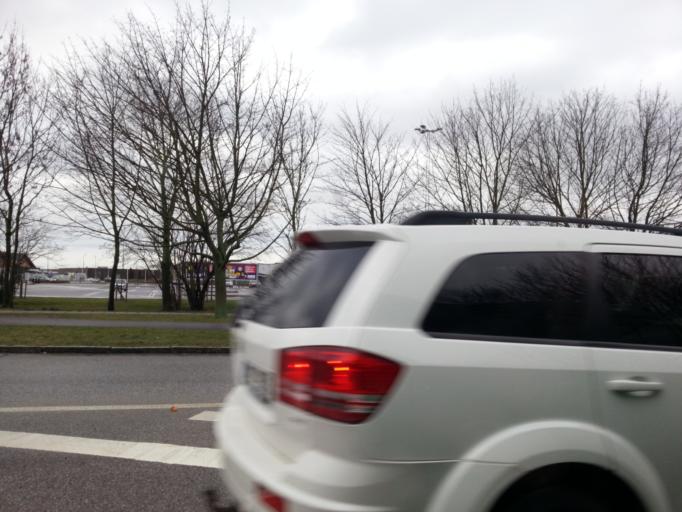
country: SE
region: Skane
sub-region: Lunds Kommun
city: Lund
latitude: 55.7185
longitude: 13.1653
